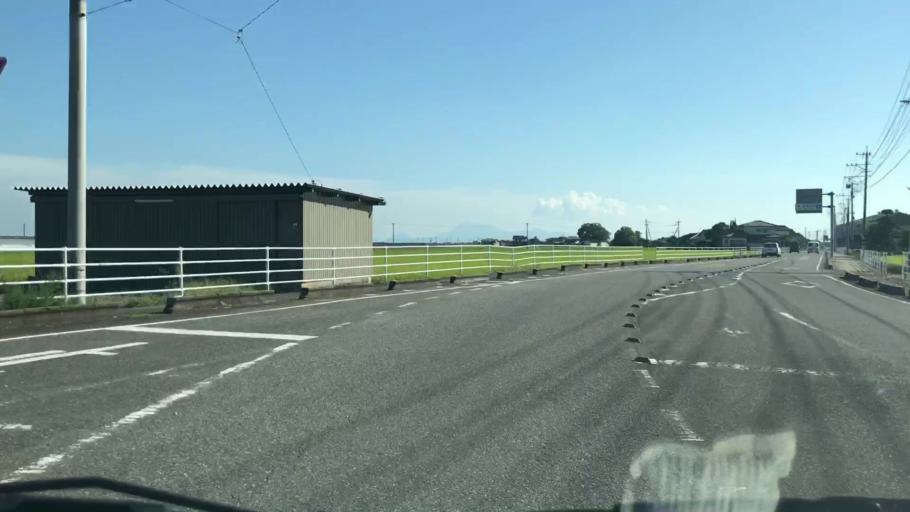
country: JP
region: Saga Prefecture
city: Okawa
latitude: 33.1963
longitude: 130.3350
